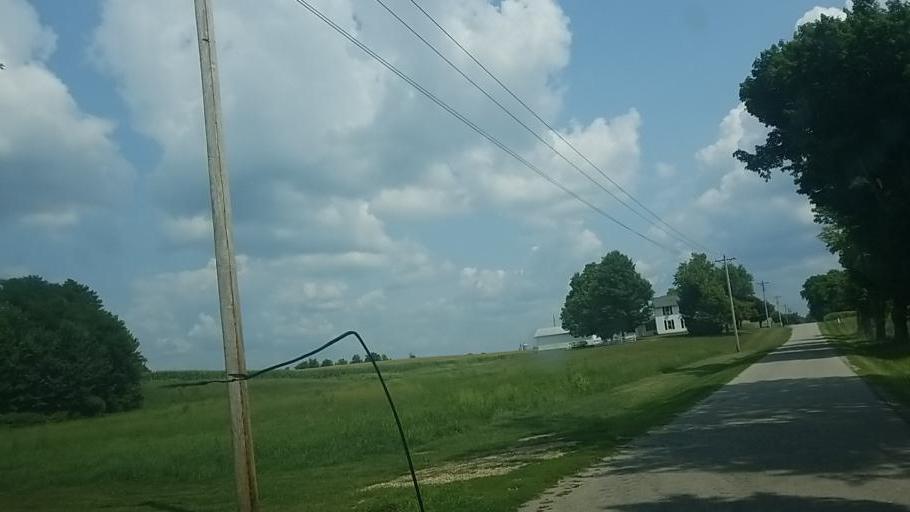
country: US
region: Ohio
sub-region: Wyandot County
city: Upper Sandusky
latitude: 40.9209
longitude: -83.1457
